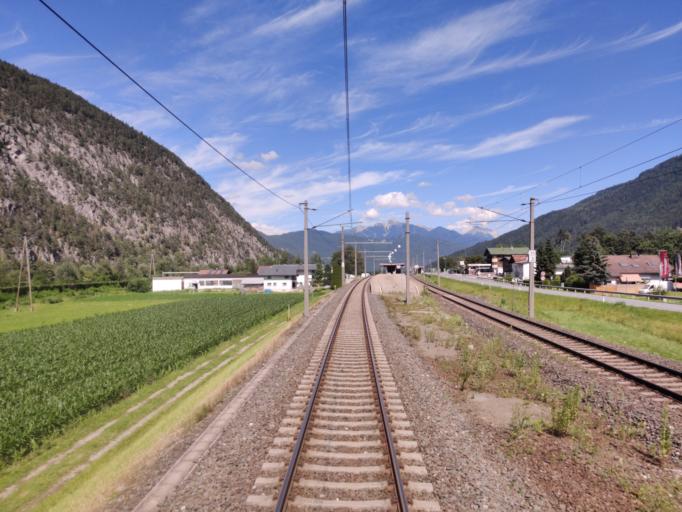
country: AT
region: Tyrol
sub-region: Politischer Bezirk Innsbruck Land
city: Wildermieming
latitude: 47.2916
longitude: 11.0214
